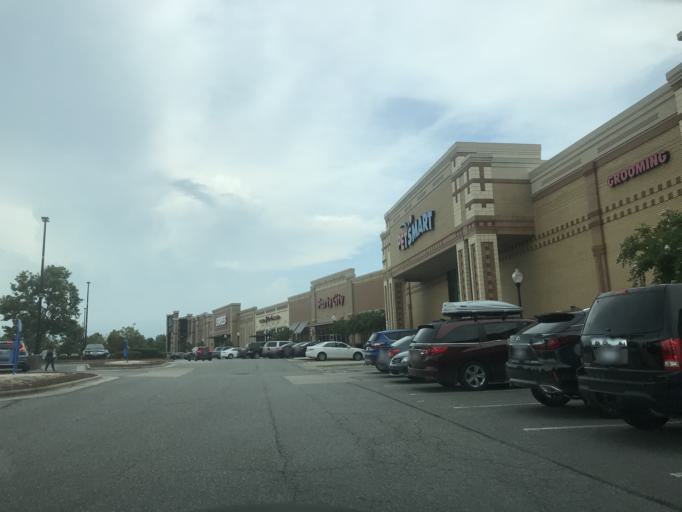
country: US
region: North Carolina
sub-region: Wake County
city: Morrisville
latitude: 35.9093
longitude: -78.7821
